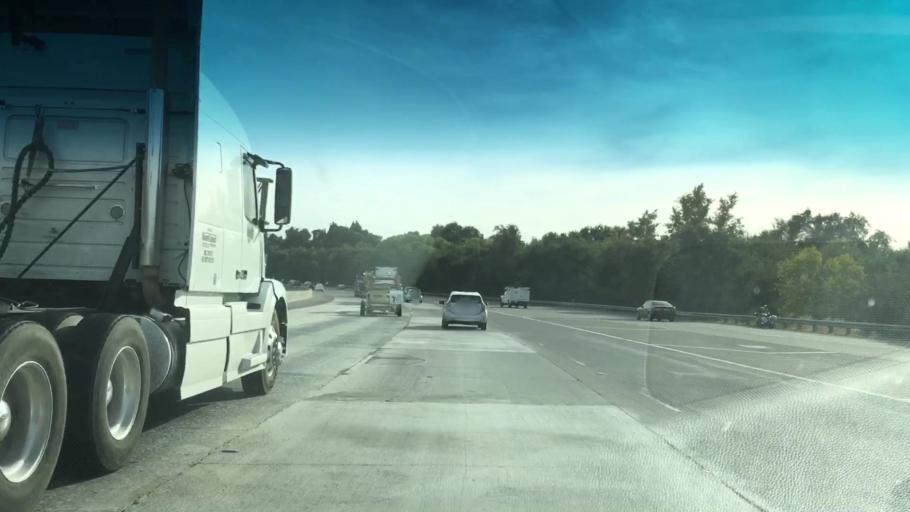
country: US
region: California
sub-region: Yolo County
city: West Sacramento
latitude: 38.5635
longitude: -121.5147
